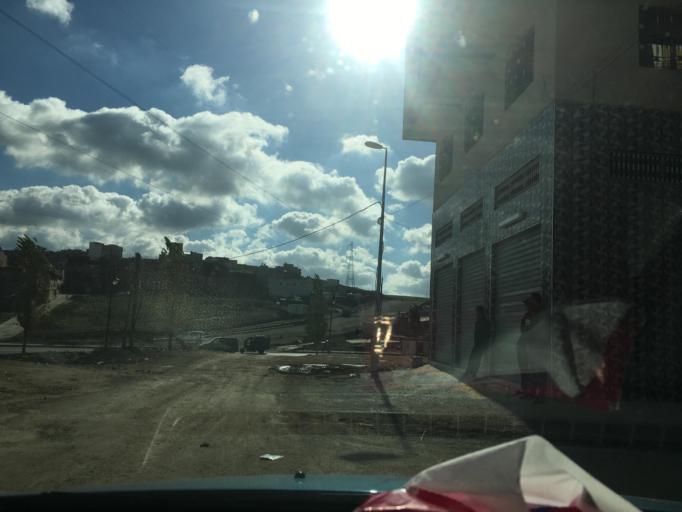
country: MA
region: Tanger-Tetouan
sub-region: Tanger-Assilah
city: Tangier
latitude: 35.7217
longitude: -5.8129
